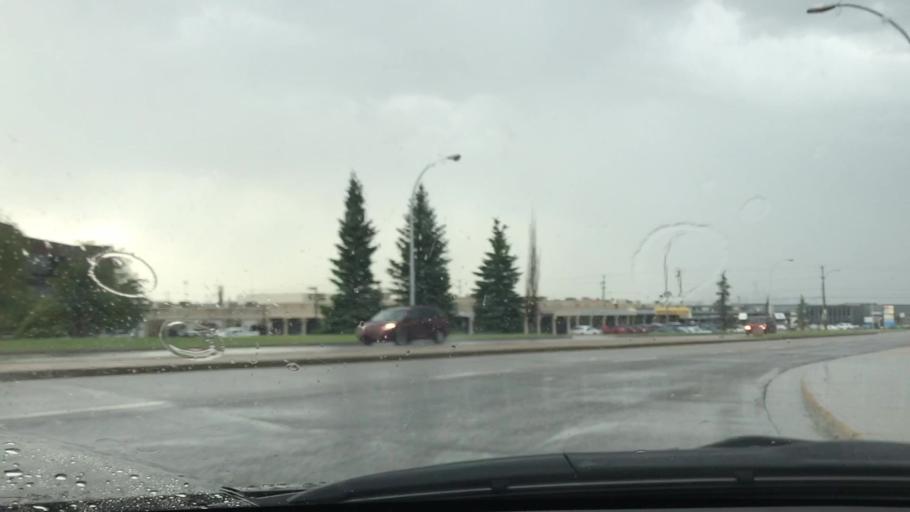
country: CA
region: Alberta
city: Edmonton
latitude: 53.4883
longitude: -113.4541
